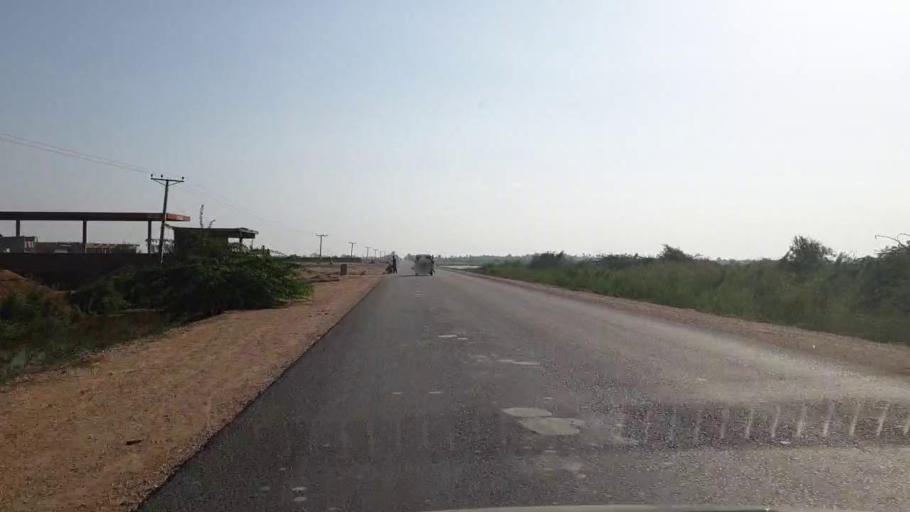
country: PK
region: Sindh
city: Badin
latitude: 24.6583
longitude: 68.9595
